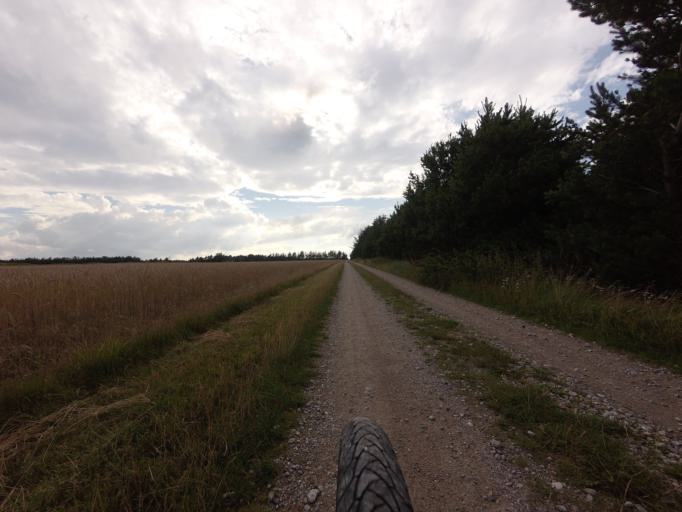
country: DK
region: North Denmark
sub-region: Hjorring Kommune
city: Hjorring
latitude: 57.4991
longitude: 9.9001
